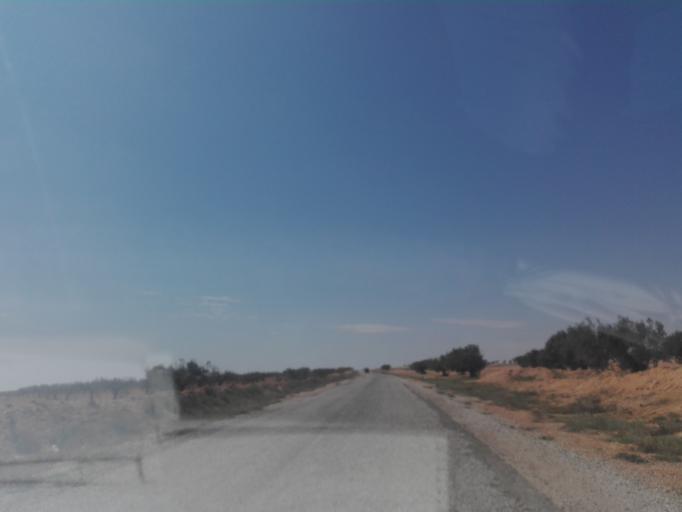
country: TN
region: Safaqis
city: Bi'r `Ali Bin Khalifah
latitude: 34.6451
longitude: 10.4098
